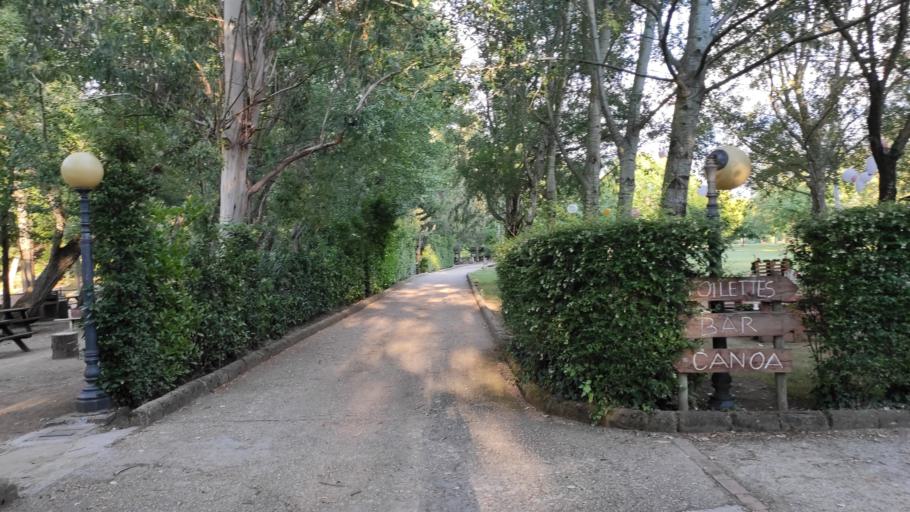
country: IT
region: Campania
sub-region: Provincia di Benevento
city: Telese
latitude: 41.2246
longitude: 14.5154
